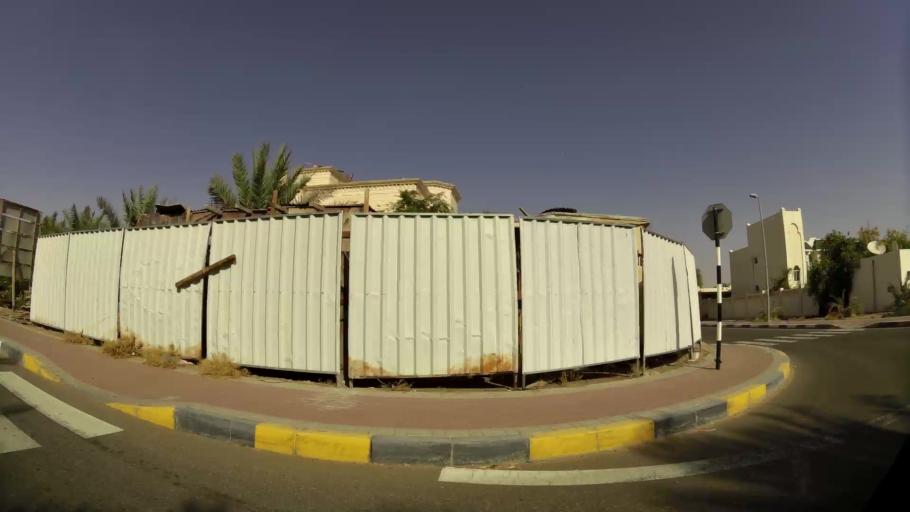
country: OM
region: Al Buraimi
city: Al Buraymi
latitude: 24.3442
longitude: 55.7978
